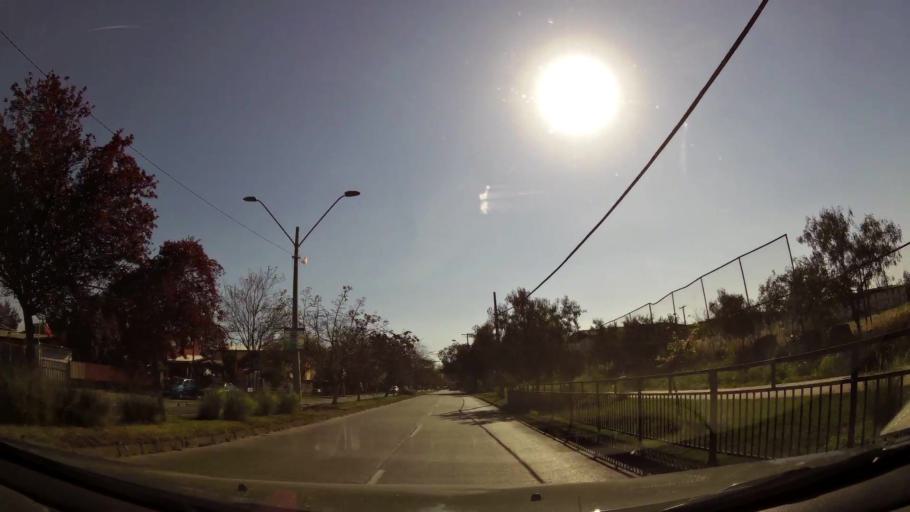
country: CL
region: Santiago Metropolitan
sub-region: Provincia de Santiago
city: La Pintana
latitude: -33.5844
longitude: -70.6467
